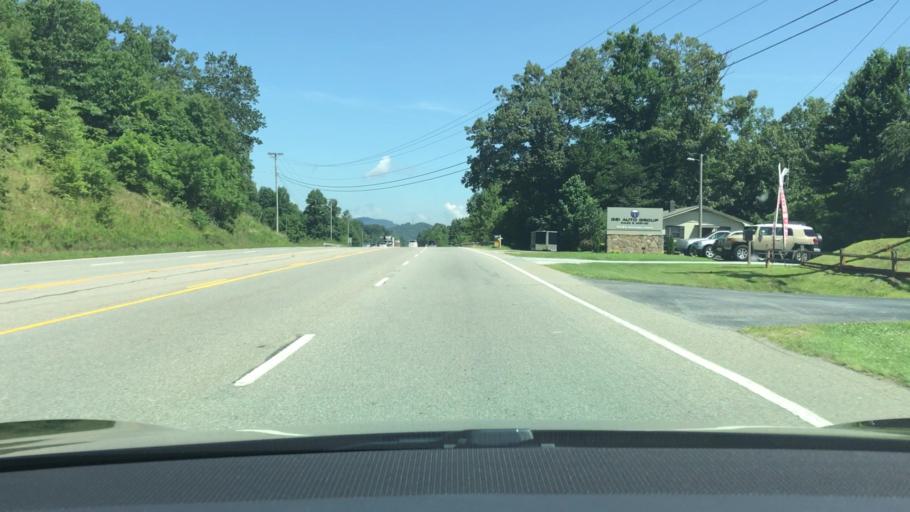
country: US
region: North Carolina
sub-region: Macon County
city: Franklin
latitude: 35.1045
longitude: -83.3862
